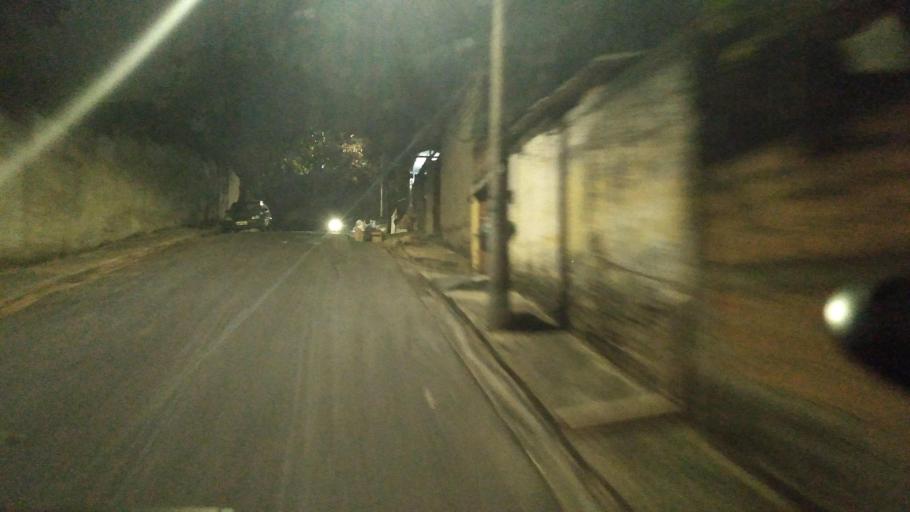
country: BR
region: Minas Gerais
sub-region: Belo Horizonte
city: Belo Horizonte
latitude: -19.8897
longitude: -43.9606
